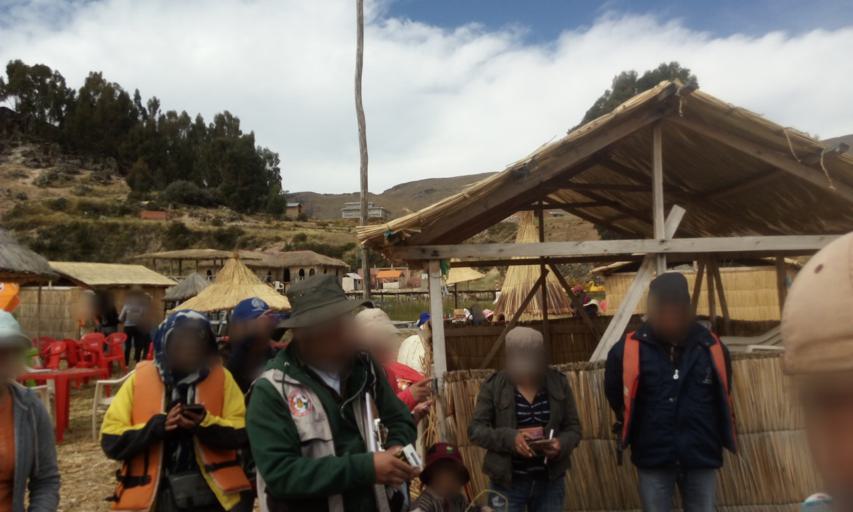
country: PE
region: Puno
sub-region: Yunguyo
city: Yunguyo
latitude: -16.1351
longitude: -69.0878
